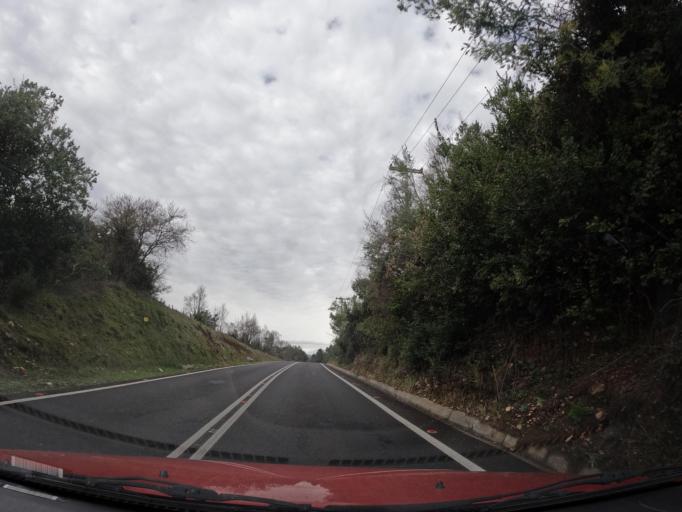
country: CL
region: Maule
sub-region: Provincia de Linares
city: Linares
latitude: -35.9139
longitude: -71.4731
